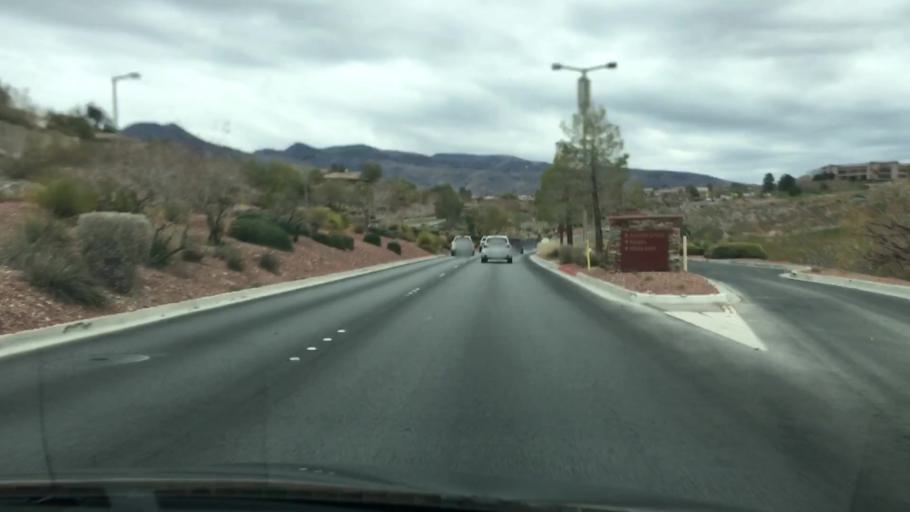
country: US
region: Nevada
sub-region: Clark County
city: Whitney
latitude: 35.9625
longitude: -115.0974
